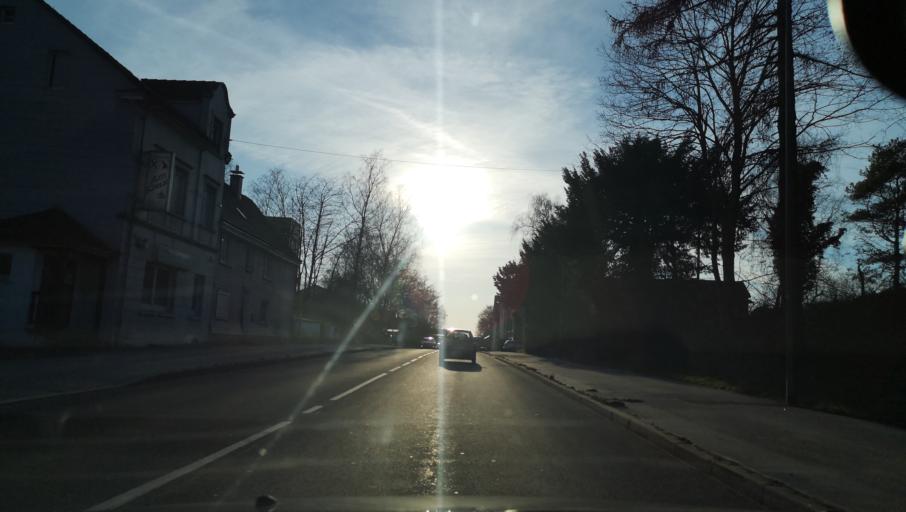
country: DE
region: North Rhine-Westphalia
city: Radevormwald
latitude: 51.2020
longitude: 7.3451
